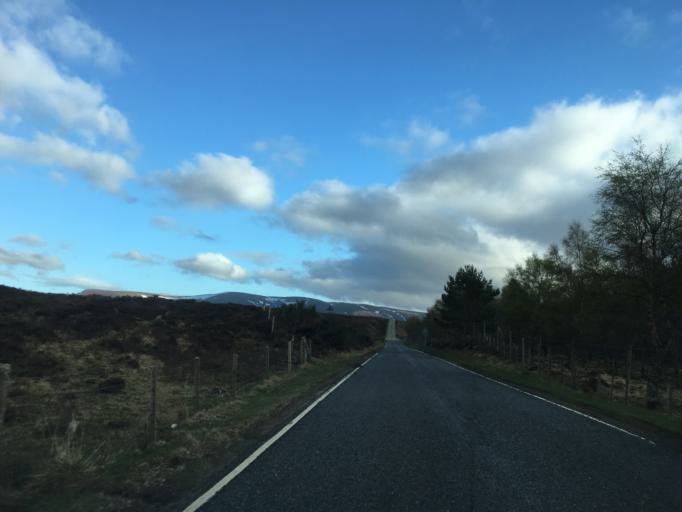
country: GB
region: Scotland
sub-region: Highland
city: Kingussie
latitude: 56.9832
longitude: -4.2379
